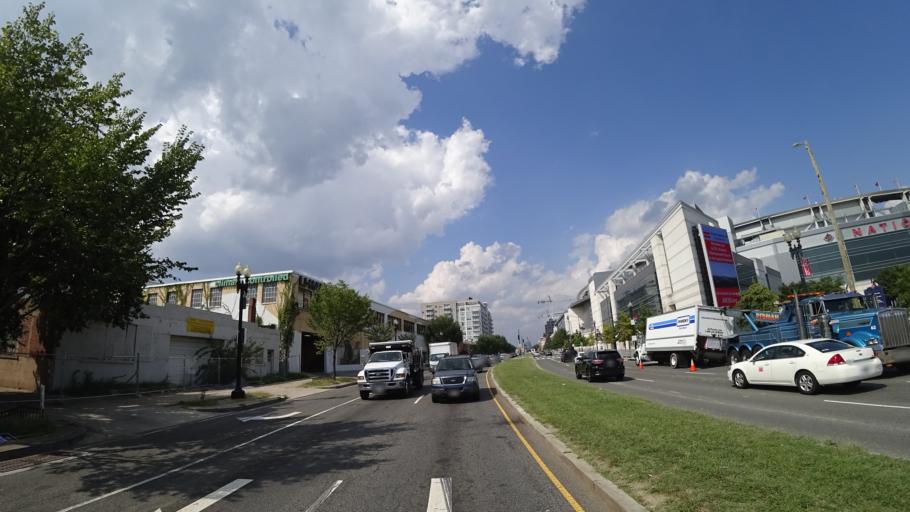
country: US
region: Washington, D.C.
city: Washington, D.C.
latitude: 38.8711
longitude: -77.0090
